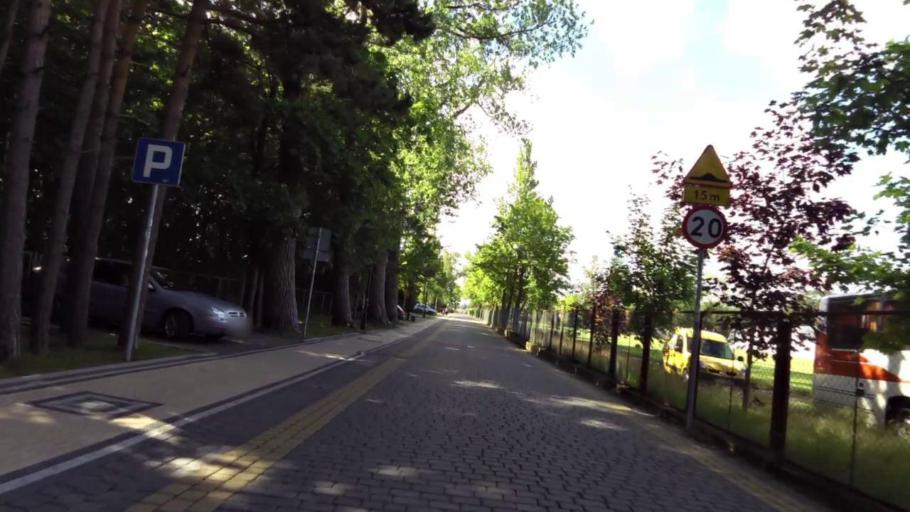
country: PL
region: West Pomeranian Voivodeship
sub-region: Powiat koszalinski
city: Mielno
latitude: 54.2636
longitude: 16.0680
